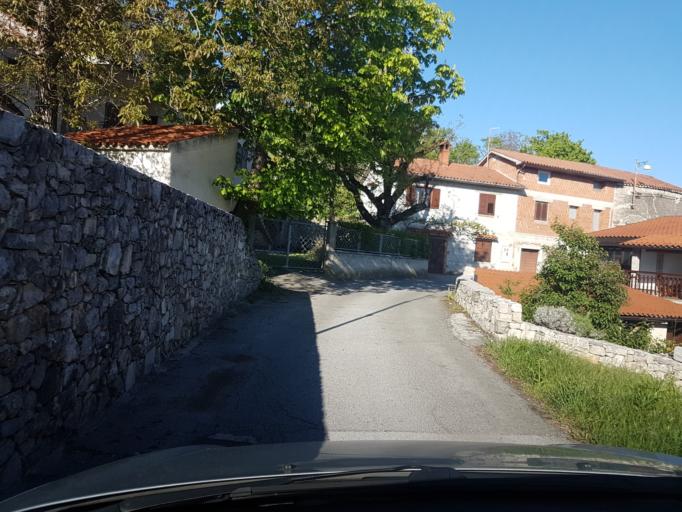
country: SI
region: Divaca
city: Divaca
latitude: 45.6634
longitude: 13.9920
